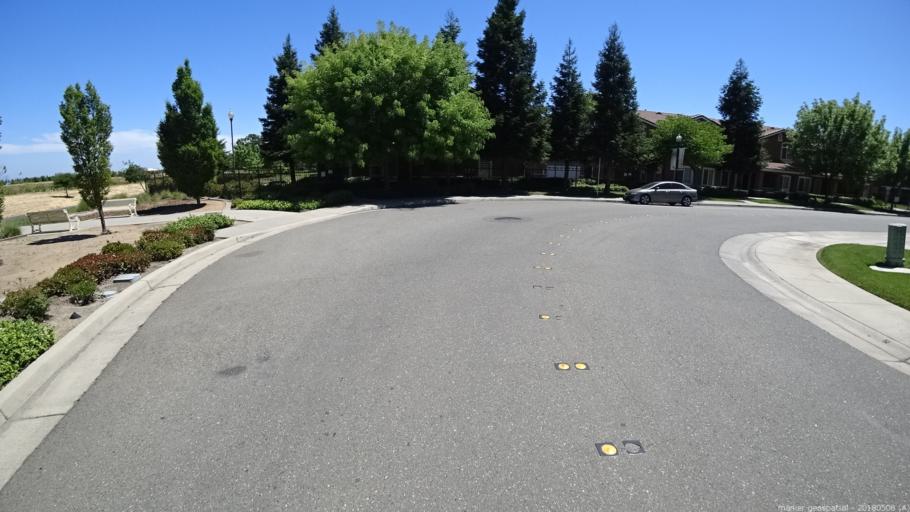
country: US
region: California
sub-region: Sacramento County
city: Elverta
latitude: 38.6617
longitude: -121.5243
